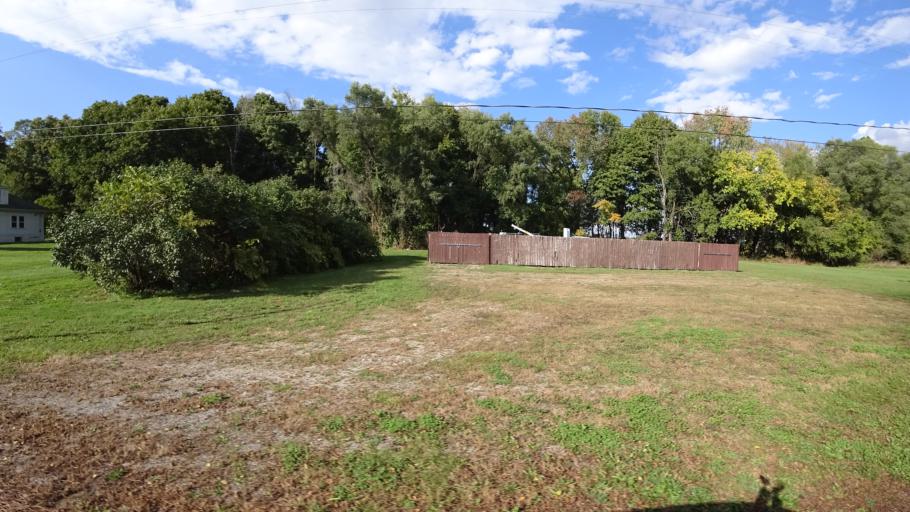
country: US
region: Michigan
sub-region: Saint Joseph County
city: Three Rivers
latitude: 41.9475
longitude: -85.6096
